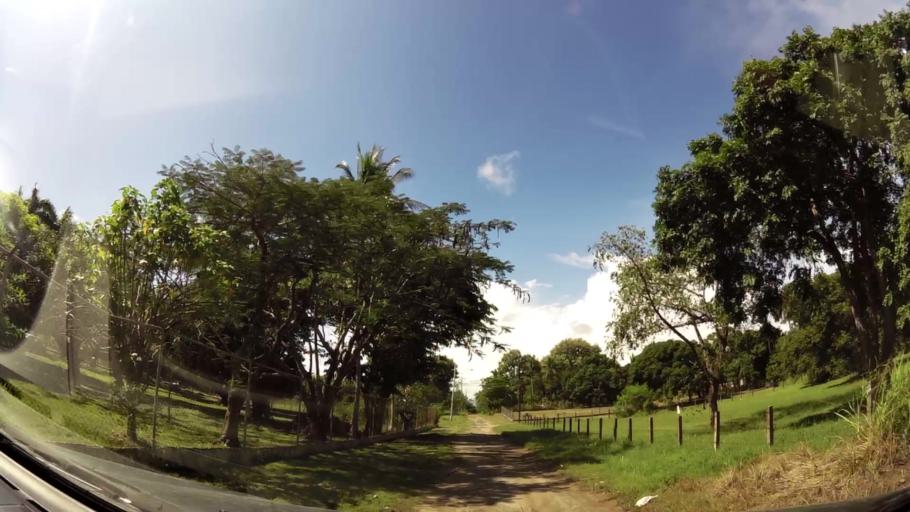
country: PA
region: Panama
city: Nueva Gorgona
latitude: 8.5569
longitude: -79.8669
